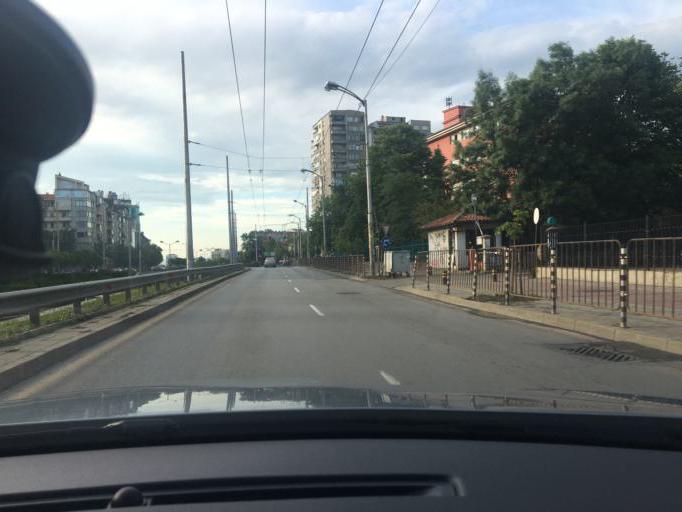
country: BG
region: Sofia-Capital
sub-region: Stolichna Obshtina
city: Sofia
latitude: 42.6830
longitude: 23.3015
